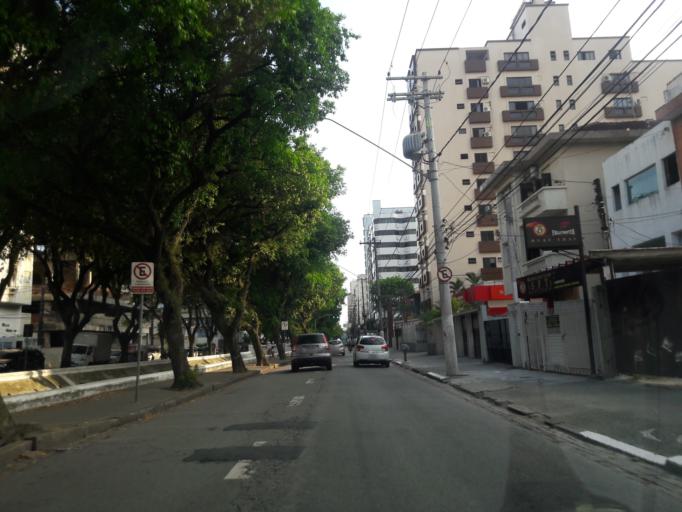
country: BR
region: Sao Paulo
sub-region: Santos
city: Santos
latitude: -23.9629
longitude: -46.3386
